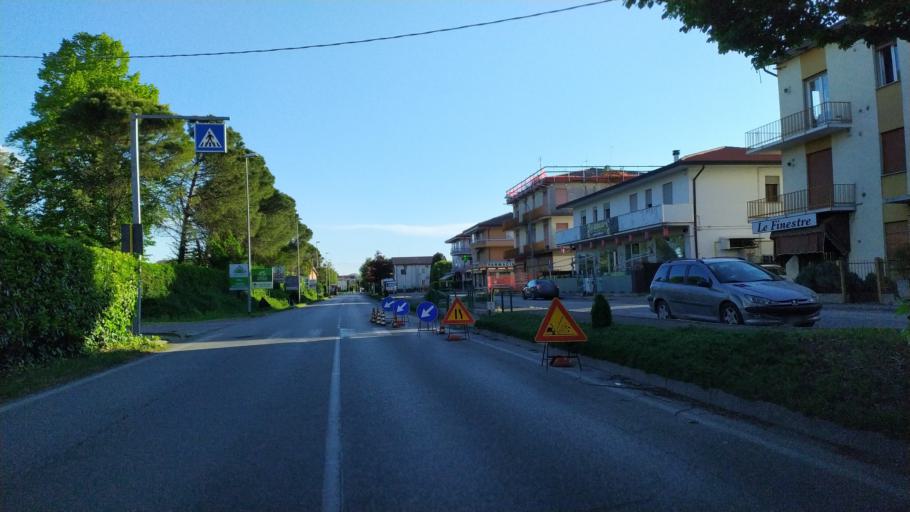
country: IT
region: Veneto
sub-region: Provincia di Padova
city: Tencarola
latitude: 45.3870
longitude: 11.8043
